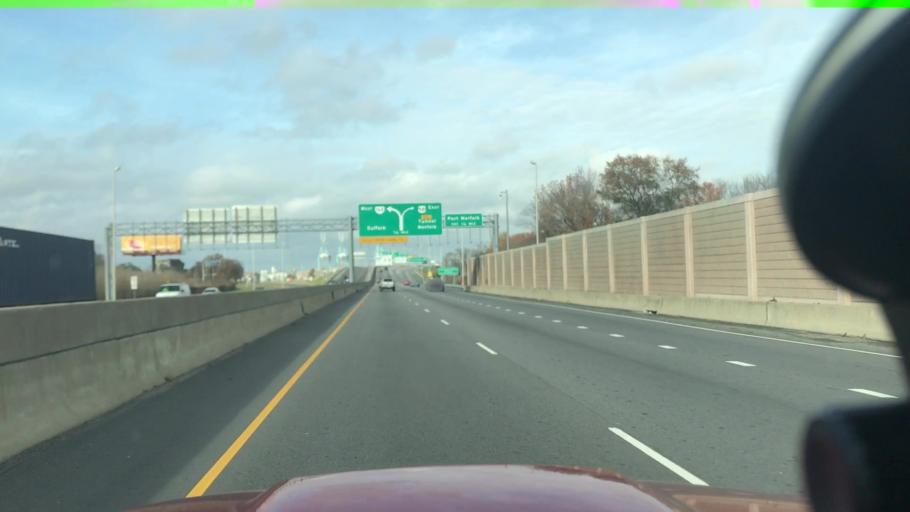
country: US
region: Virginia
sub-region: City of Portsmouth
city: Portsmouth
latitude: 36.8402
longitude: -76.3291
